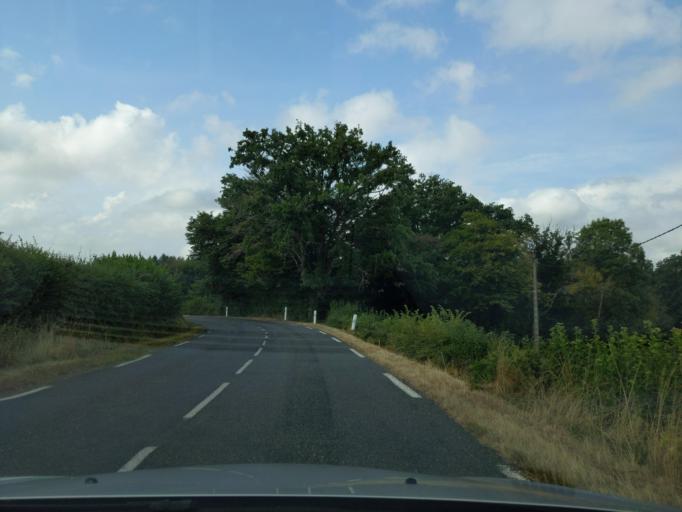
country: FR
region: Bourgogne
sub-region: Departement de la Nievre
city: Luzy
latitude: 46.7197
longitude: 3.8827
